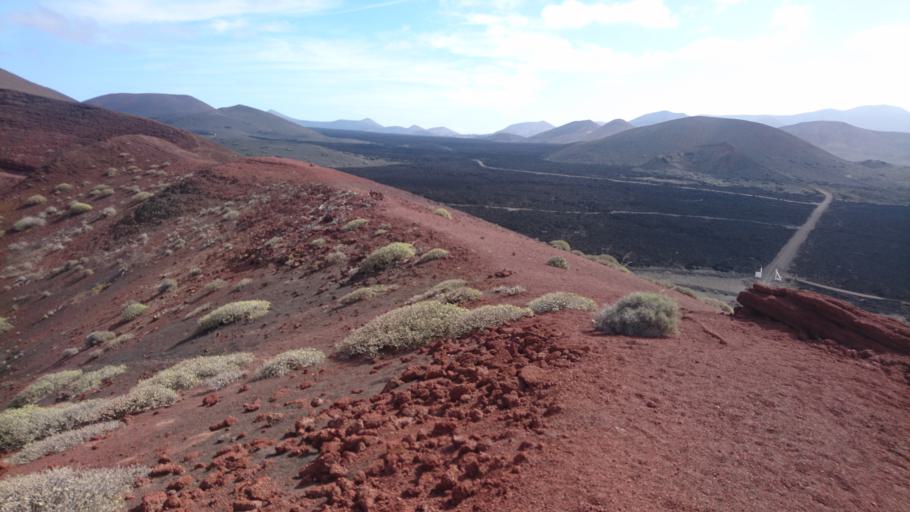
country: ES
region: Canary Islands
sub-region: Provincia de Las Palmas
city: Yaiza
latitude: 28.9881
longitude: -13.8158
